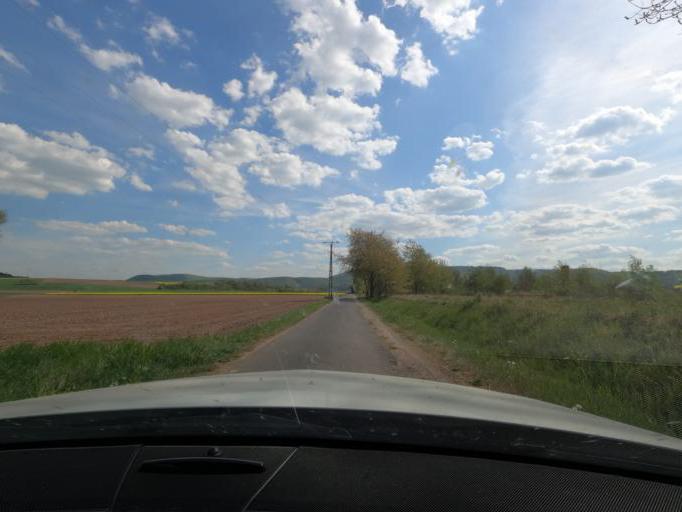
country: DE
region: Hesse
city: Wanfried
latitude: 51.1460
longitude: 10.1835
